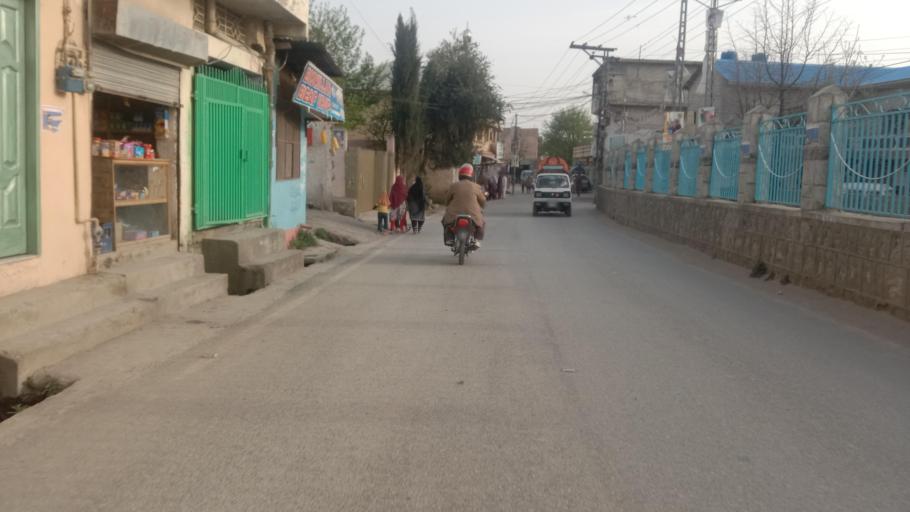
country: PK
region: Khyber Pakhtunkhwa
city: Abbottabad
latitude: 34.1663
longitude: 73.2597
